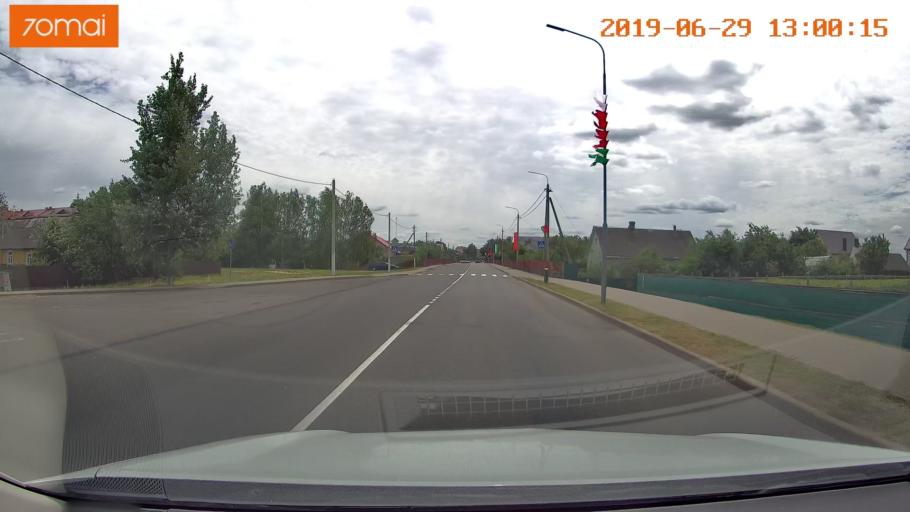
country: BY
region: Minsk
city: Slutsk
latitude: 53.0461
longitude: 27.5563
